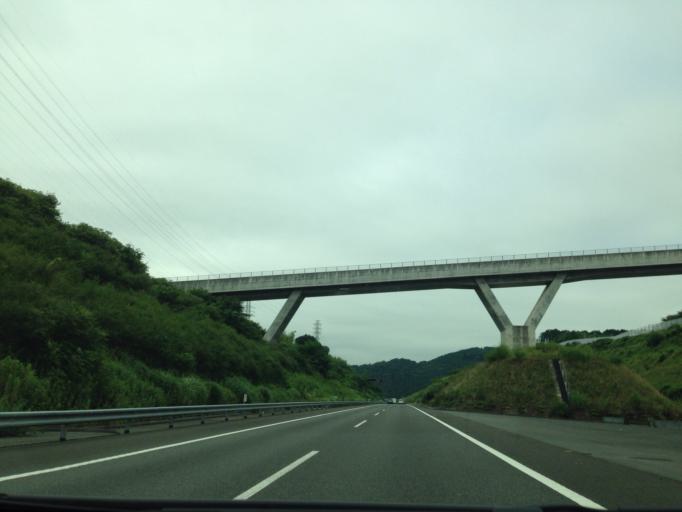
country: JP
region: Shizuoka
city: Fujinomiya
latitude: 35.1918
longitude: 138.6291
